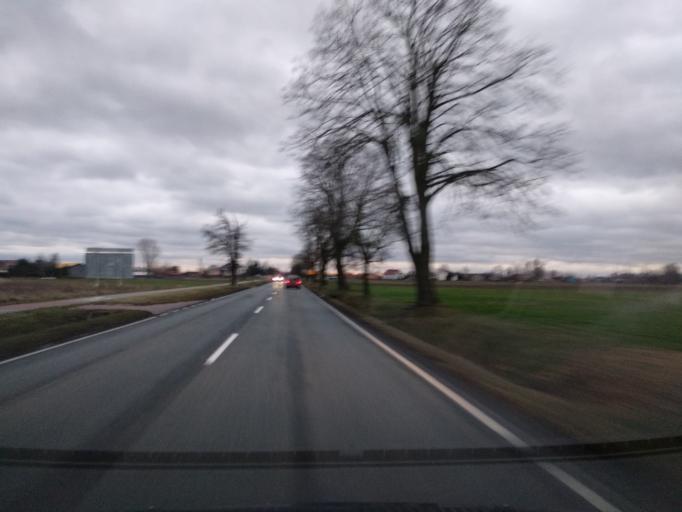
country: PL
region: Greater Poland Voivodeship
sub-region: Powiat koninski
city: Rychwal
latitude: 52.0849
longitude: 18.1626
